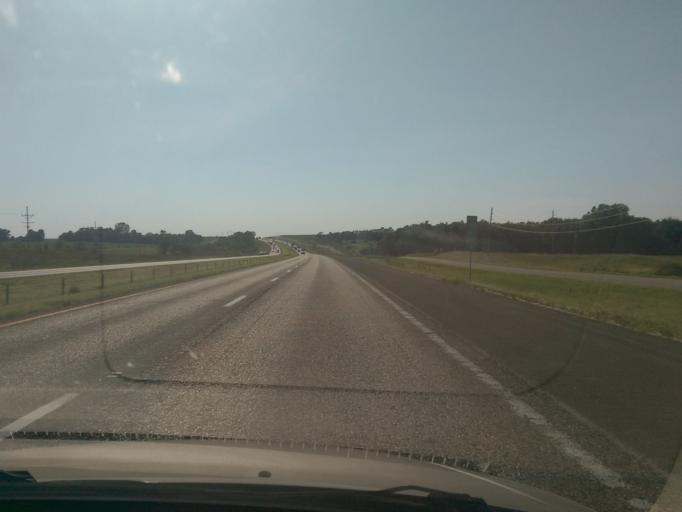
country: US
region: Missouri
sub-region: Lafayette County
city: Concordia
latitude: 38.9863
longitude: -93.5015
